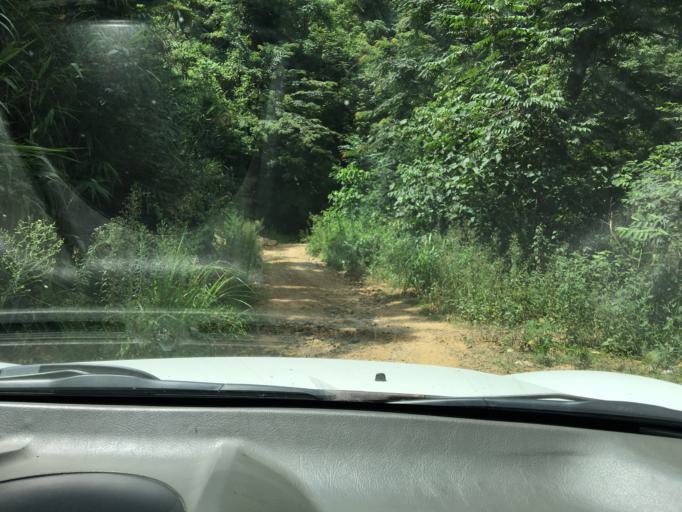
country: CN
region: Guangxi Zhuangzu Zizhiqu
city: Tongle
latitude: 24.9704
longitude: 105.9774
